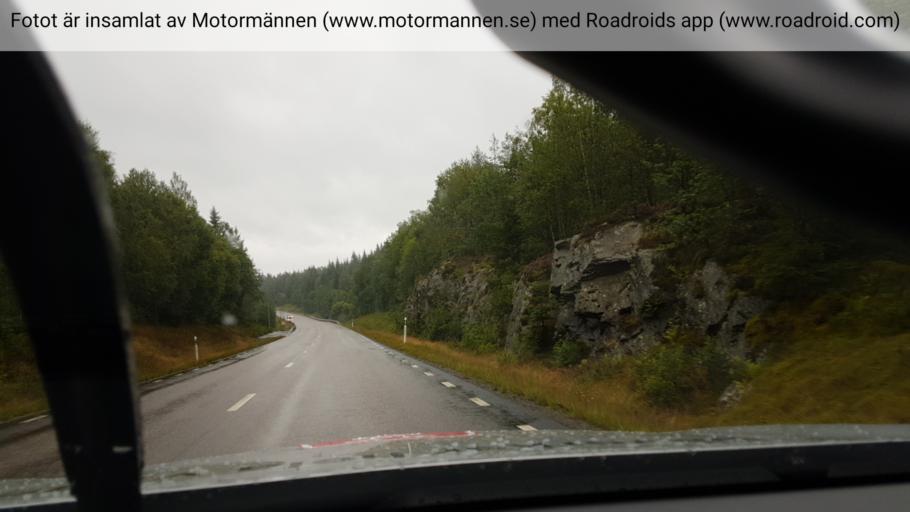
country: SE
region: Vaestra Goetaland
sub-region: Dals-Ed Kommun
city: Ed
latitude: 58.8757
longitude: 11.8628
